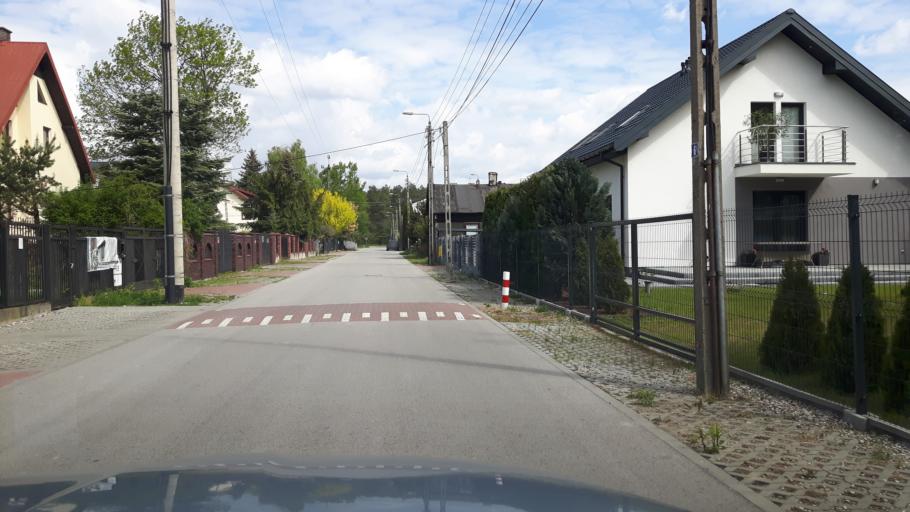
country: PL
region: Masovian Voivodeship
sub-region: Warszawa
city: Wesola
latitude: 52.2503
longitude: 21.2008
